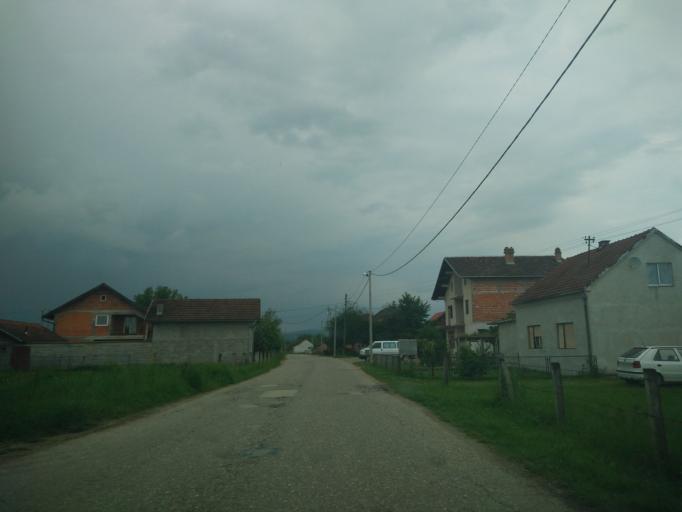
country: BA
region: Republika Srpska
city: Prijedor
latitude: 44.9445
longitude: 16.7007
